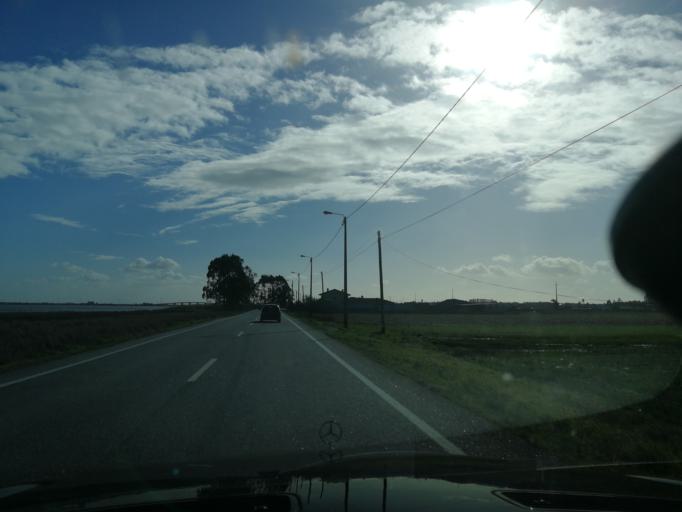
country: PT
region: Aveiro
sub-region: Estarreja
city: Pardilho
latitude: 40.8071
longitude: -8.6723
